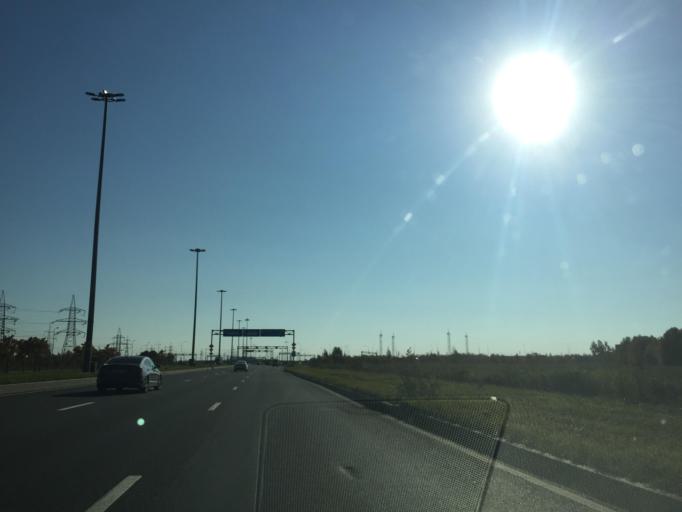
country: RU
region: St.-Petersburg
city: Metallostroy
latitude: 59.7514
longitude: 30.5265
